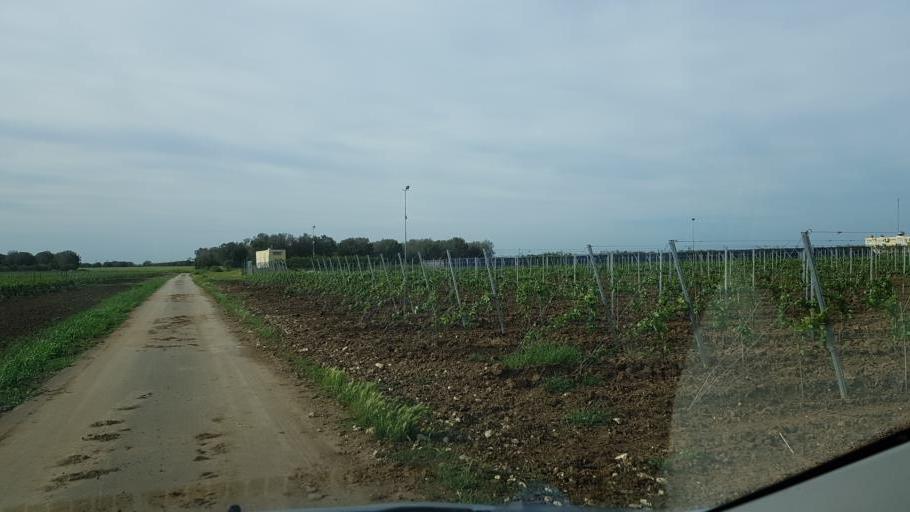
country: IT
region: Apulia
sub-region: Provincia di Brindisi
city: Tuturano
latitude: 40.5174
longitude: 17.9649
